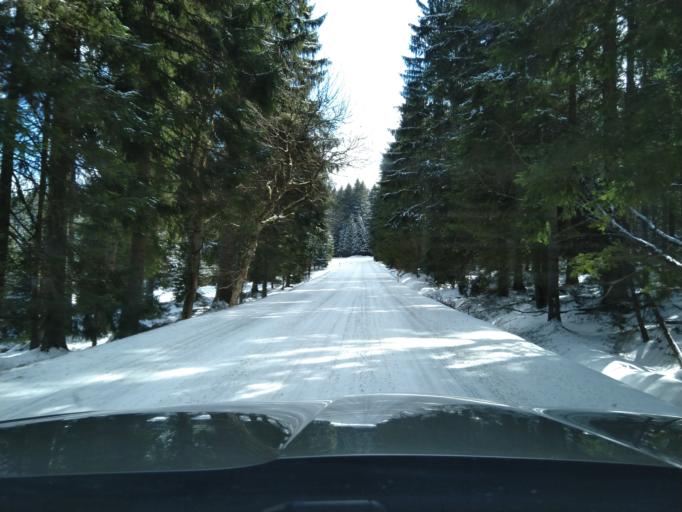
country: CZ
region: Jihocesky
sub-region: Okres Prachatice
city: Borova Lada
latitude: 49.0381
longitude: 13.5985
